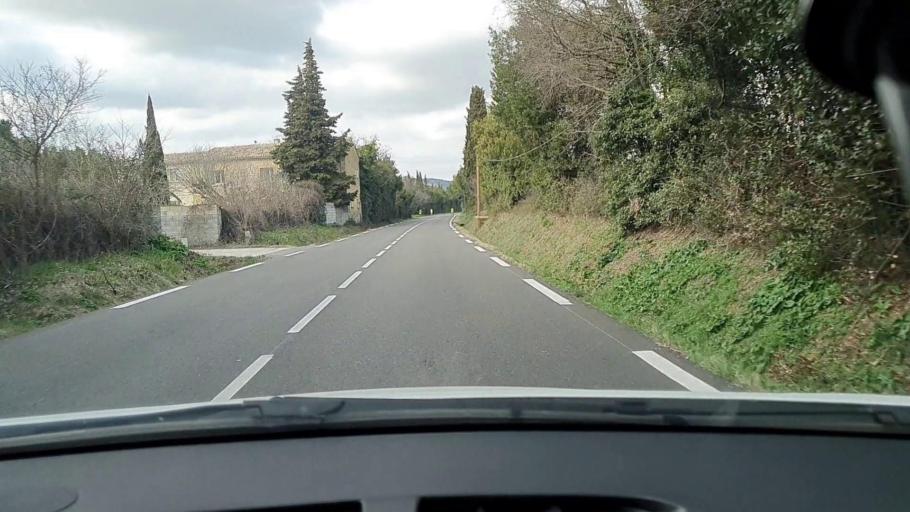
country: FR
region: Languedoc-Roussillon
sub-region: Departement du Gard
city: Sernhac
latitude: 43.9054
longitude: 4.5690
